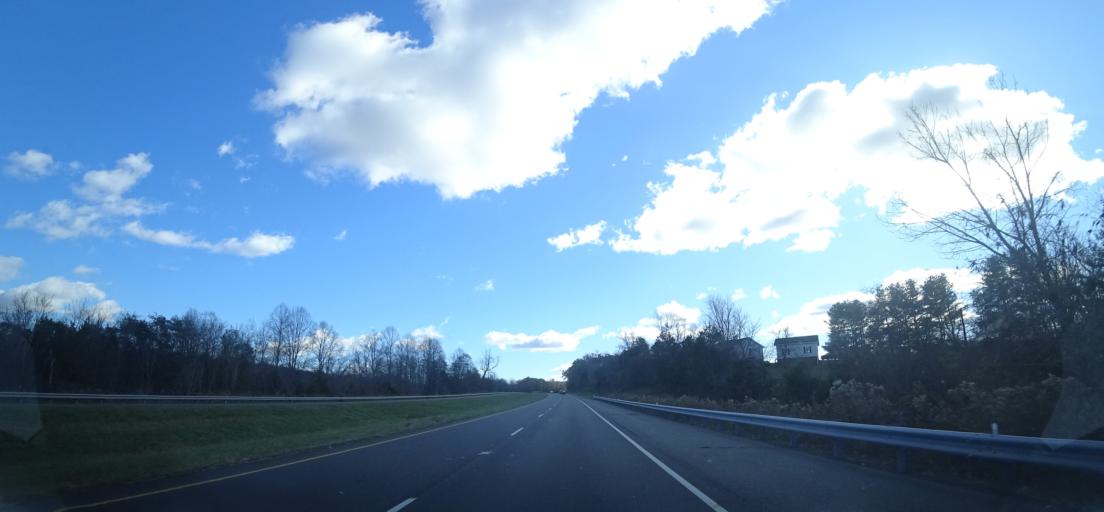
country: US
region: Virginia
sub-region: Greene County
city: Stanardsville
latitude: 38.2876
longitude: -78.4328
